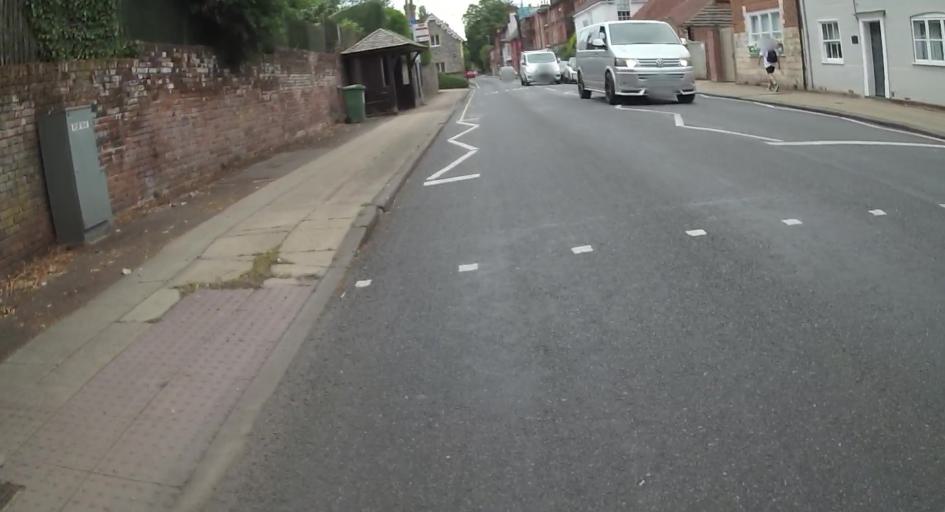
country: GB
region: England
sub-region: Hampshire
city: Winchester
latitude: 51.0487
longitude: -1.3232
